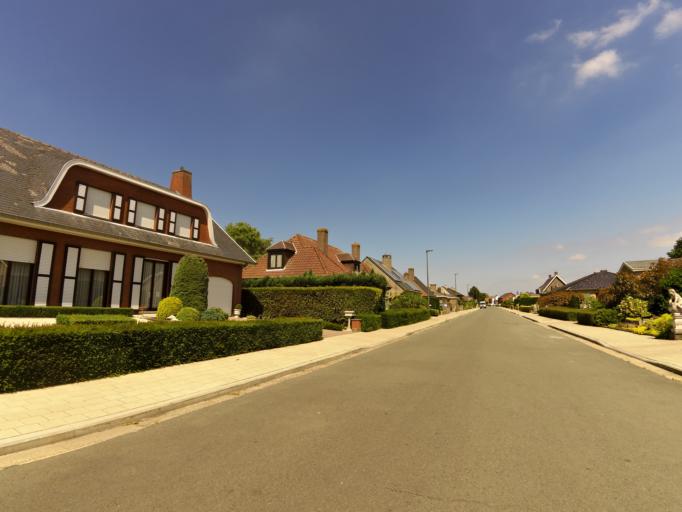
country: BE
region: Flanders
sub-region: Provincie West-Vlaanderen
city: Ichtegem
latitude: 51.1308
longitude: 3.0185
